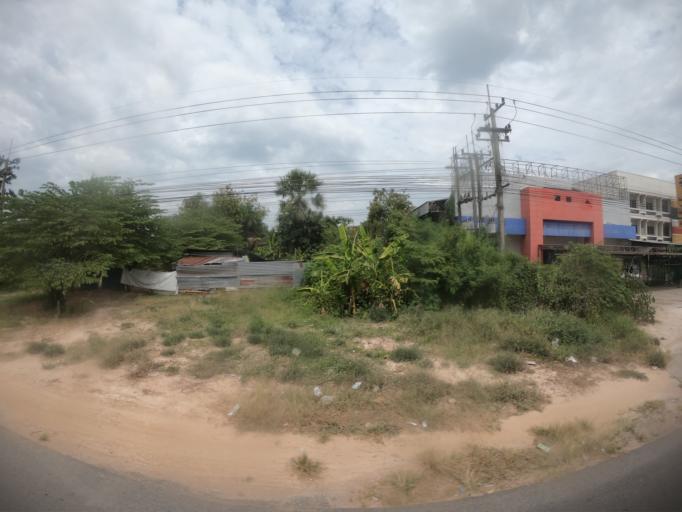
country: TH
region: Maha Sarakham
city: Maha Sarakham
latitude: 16.1621
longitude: 103.3477
